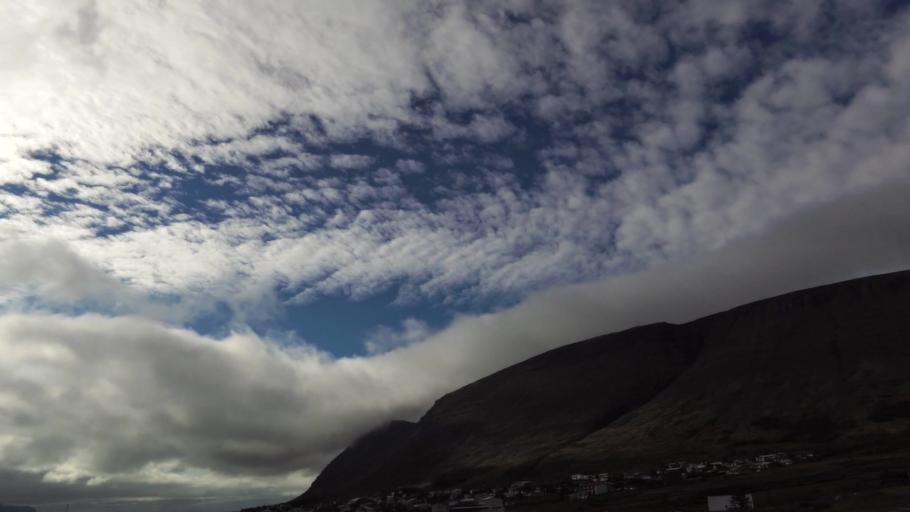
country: IS
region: West
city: Olafsvik
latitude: 65.5894
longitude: -23.9712
